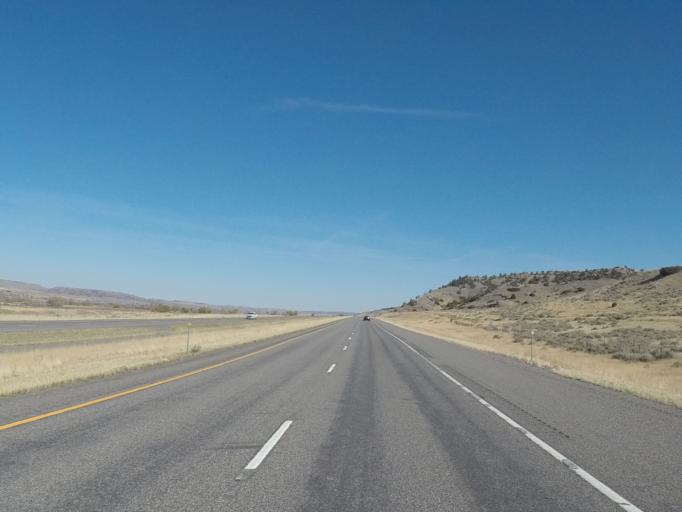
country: US
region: Montana
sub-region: Sweet Grass County
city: Big Timber
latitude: 45.7670
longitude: -110.0876
